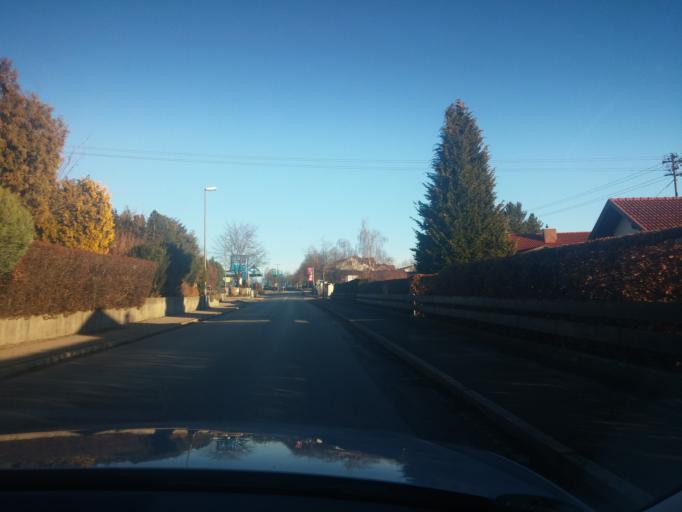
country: DE
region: Bavaria
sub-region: Swabia
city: Altusried
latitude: 47.8021
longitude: 10.2226
